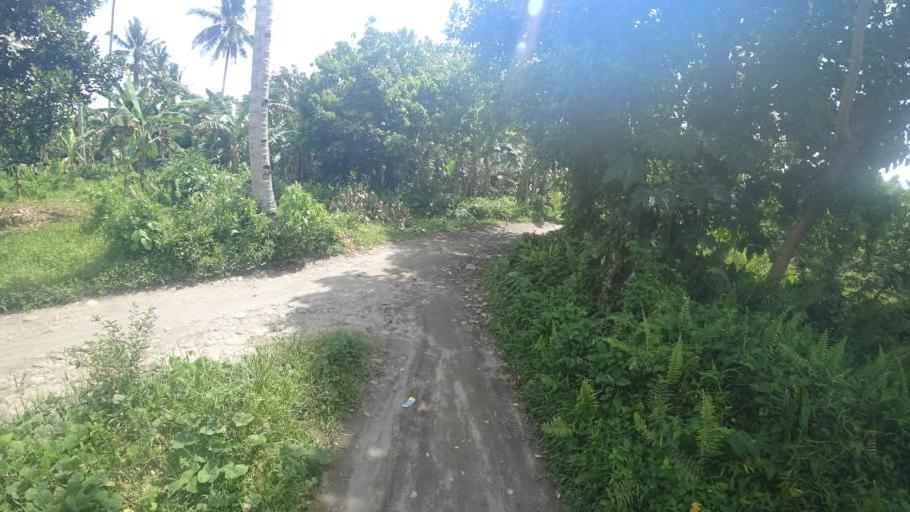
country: PH
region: Eastern Visayas
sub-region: Province of Leyte
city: Jaro
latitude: 11.2019
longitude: 124.8067
